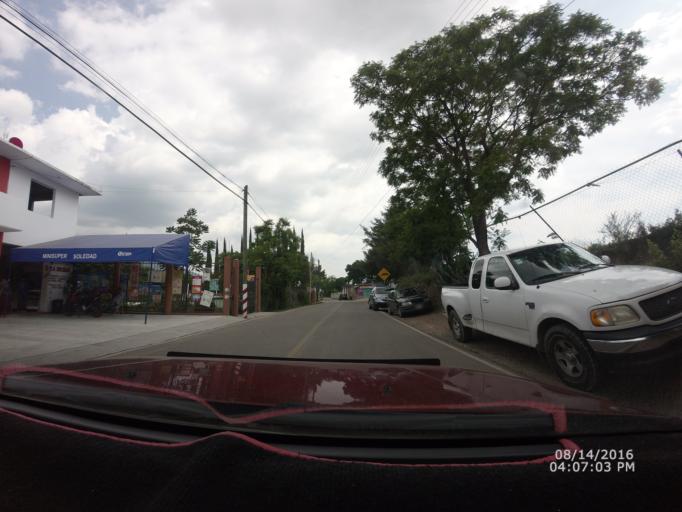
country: MX
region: Oaxaca
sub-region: San Juan Bautista Guelache
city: Fraccionamiento San Miguel
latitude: 17.1933
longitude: -96.7646
